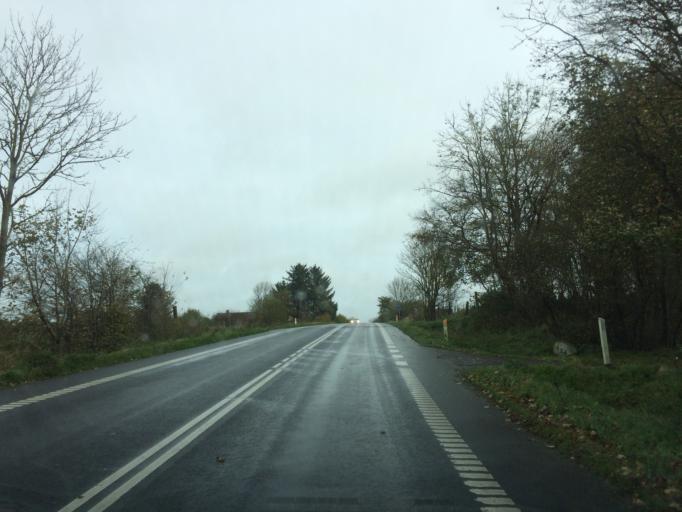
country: DK
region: South Denmark
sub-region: Fredericia Kommune
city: Taulov
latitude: 55.5248
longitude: 9.5490
